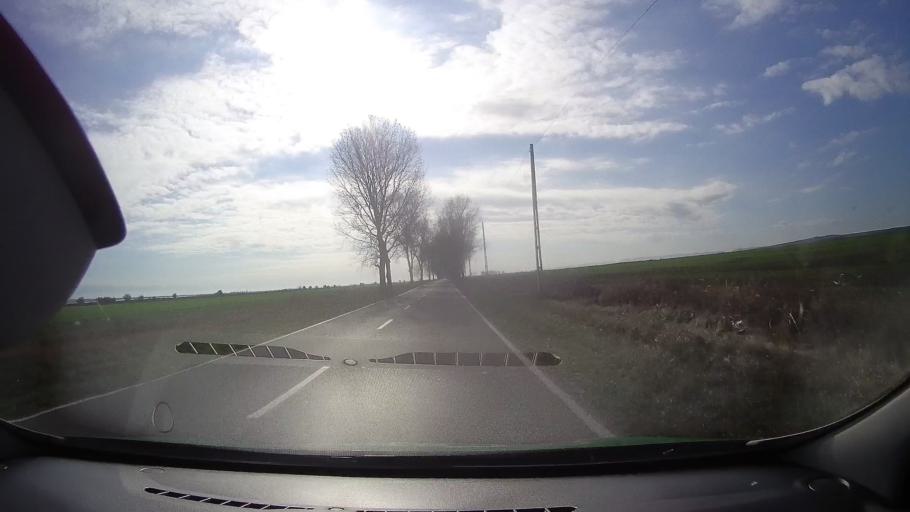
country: RO
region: Tulcea
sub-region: Comuna Valea Nucarilor
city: Agighiol
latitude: 45.0134
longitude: 28.8839
